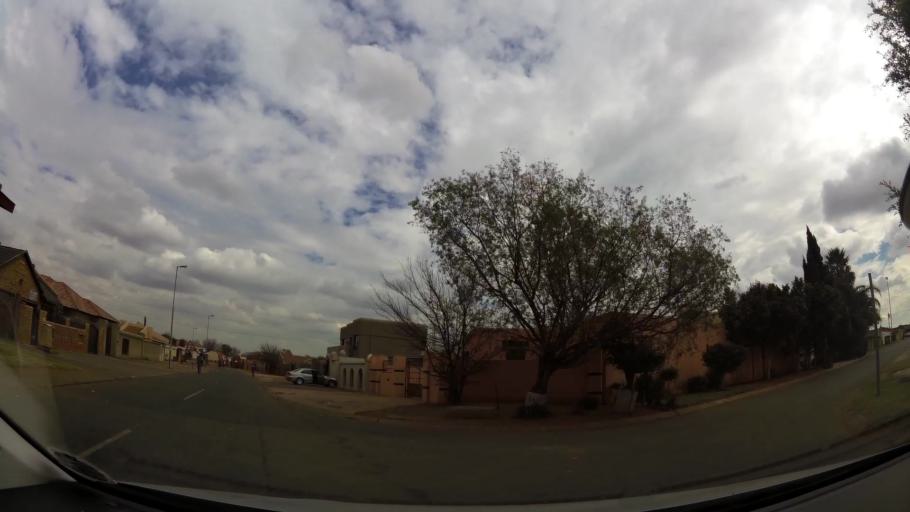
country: ZA
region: Gauteng
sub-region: City of Johannesburg Metropolitan Municipality
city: Soweto
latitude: -26.2837
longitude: 27.8510
